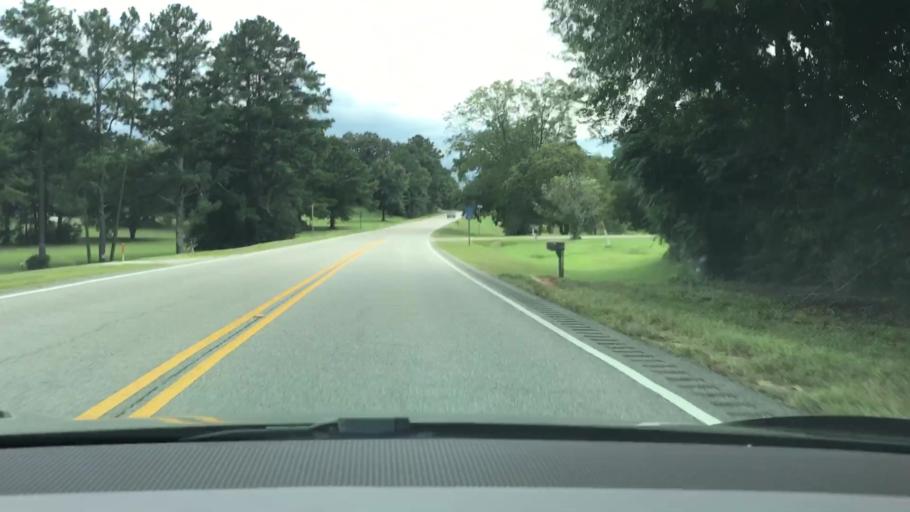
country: US
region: Alabama
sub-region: Coffee County
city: Elba
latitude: 31.5517
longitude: -86.0162
